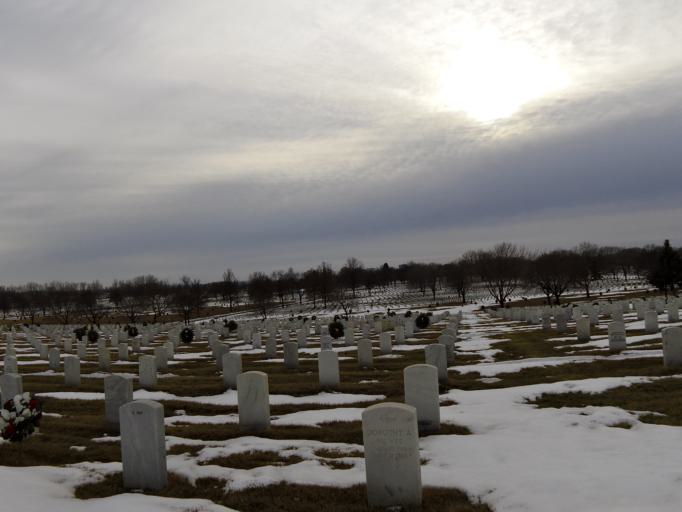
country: US
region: Minnesota
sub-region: Hennepin County
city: Richfield
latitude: 44.8754
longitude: -93.2134
